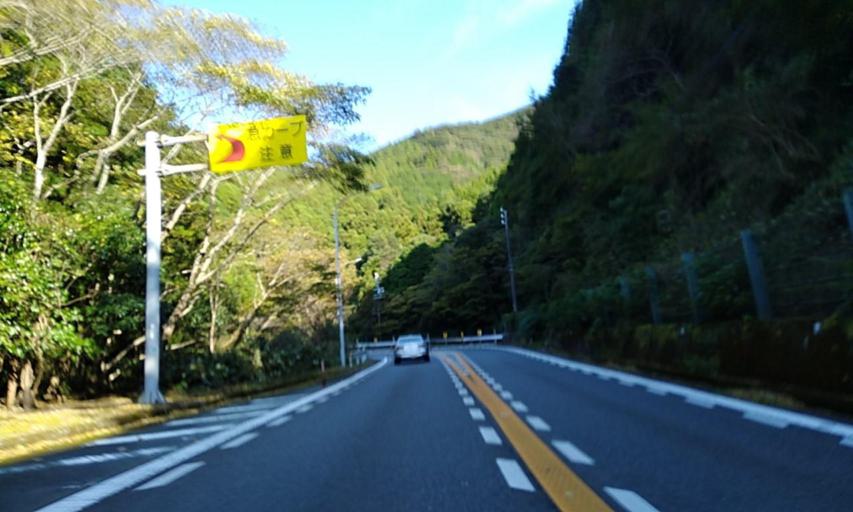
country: JP
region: Mie
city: Ise
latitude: 34.4102
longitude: 136.7677
